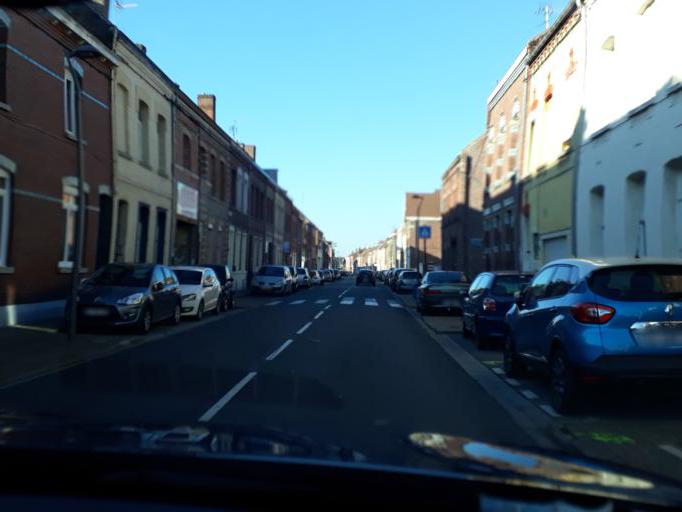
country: FR
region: Nord-Pas-de-Calais
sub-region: Departement du Nord
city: Dechy
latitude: 50.3654
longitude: 3.1067
